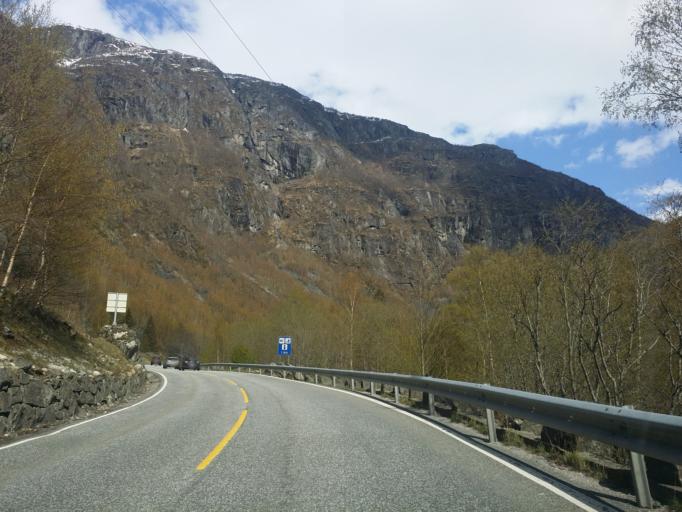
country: NO
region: Hordaland
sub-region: Eidfjord
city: Eidfjord
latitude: 60.4187
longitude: 7.1723
